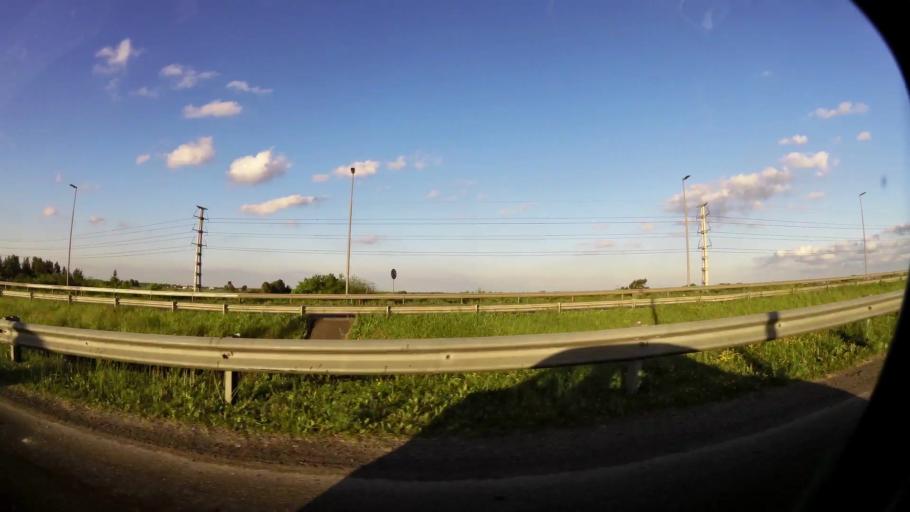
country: AR
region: Buenos Aires
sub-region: Partido de Quilmes
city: Quilmes
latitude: -34.7808
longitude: -58.1524
